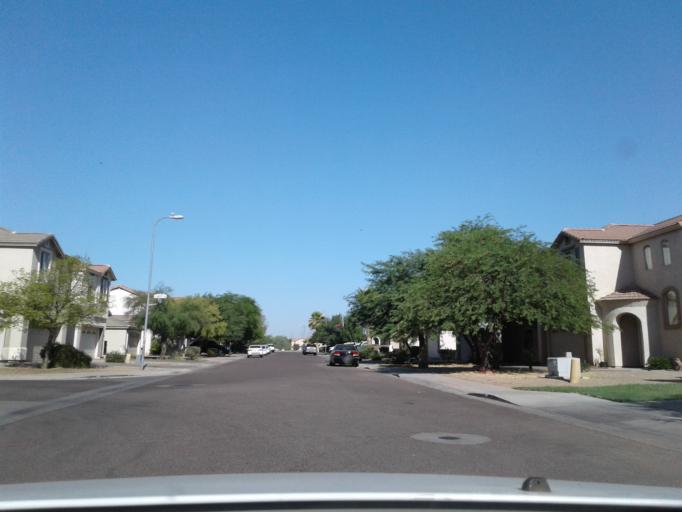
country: US
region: Arizona
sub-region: Maricopa County
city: Laveen
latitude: 33.4148
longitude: -112.1888
